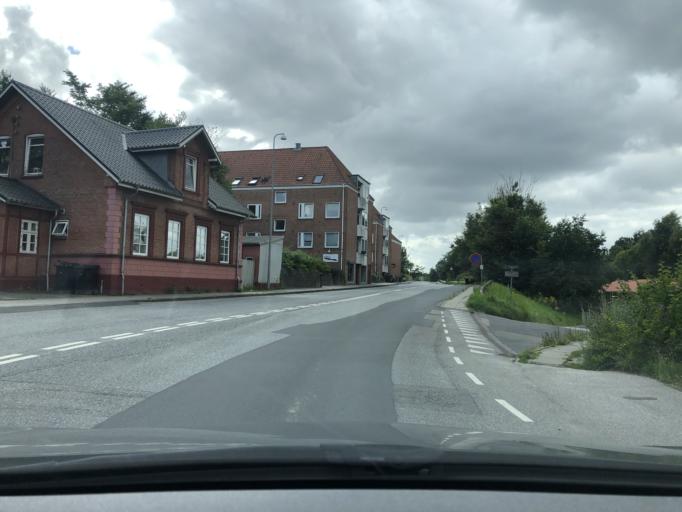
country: DK
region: South Denmark
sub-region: Vejle Kommune
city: Vejle
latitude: 55.7025
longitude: 9.5220
